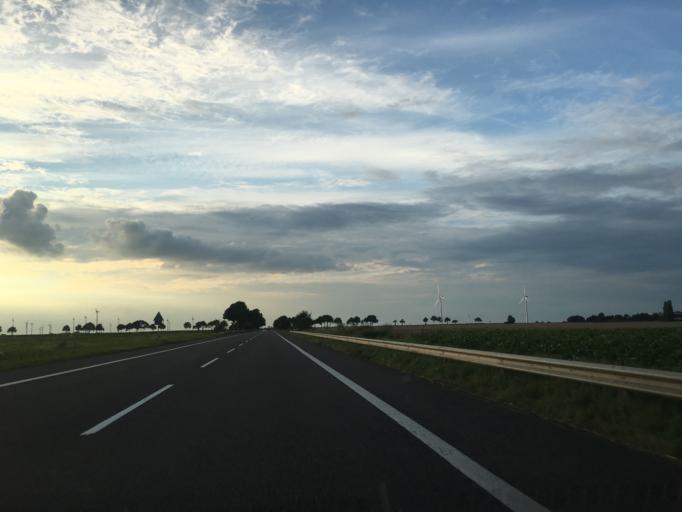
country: DE
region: North Rhine-Westphalia
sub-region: Regierungsbezirk Koln
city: Linnich
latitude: 50.9888
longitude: 6.3405
